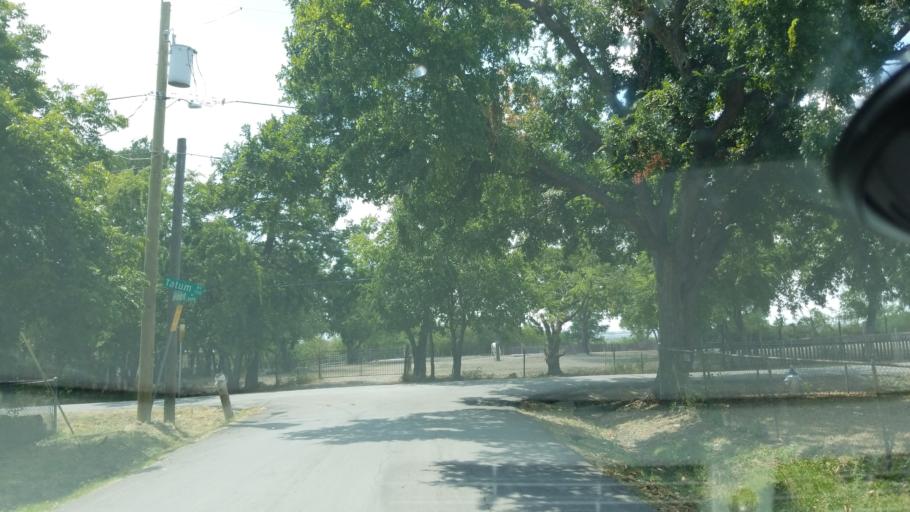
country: US
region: Texas
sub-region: Dallas County
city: Cockrell Hill
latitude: 32.7512
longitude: -96.9151
